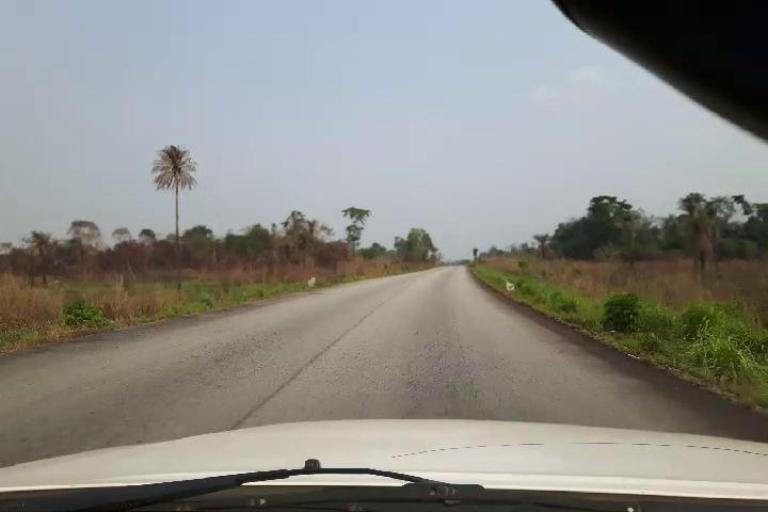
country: SL
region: Southern Province
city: Baiima
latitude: 8.1525
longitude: -11.9134
